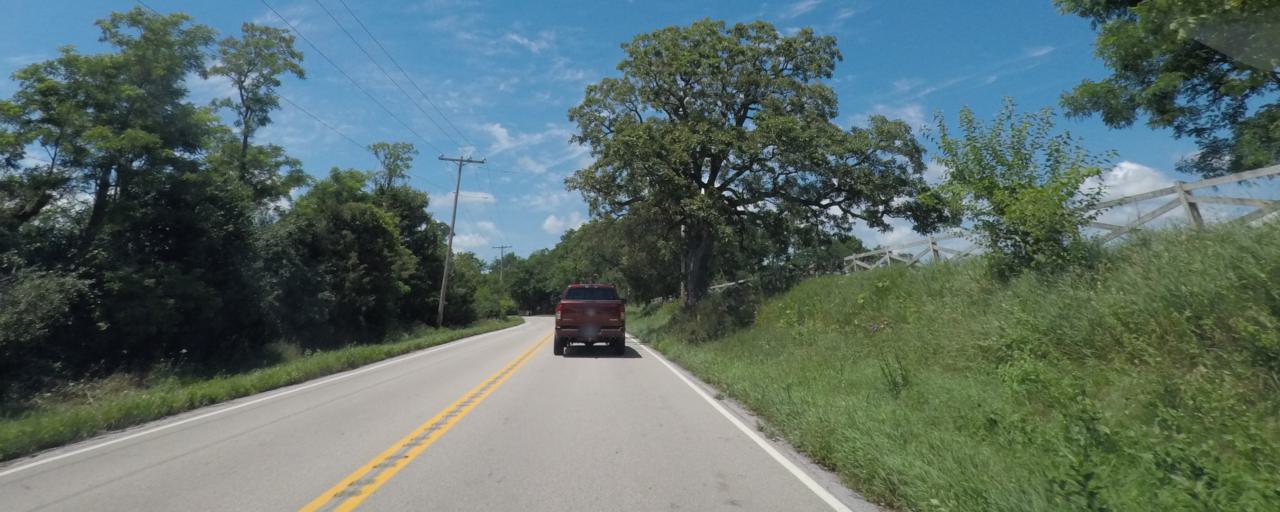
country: US
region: Wisconsin
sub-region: Jefferson County
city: Palmyra
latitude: 42.9270
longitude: -88.5312
